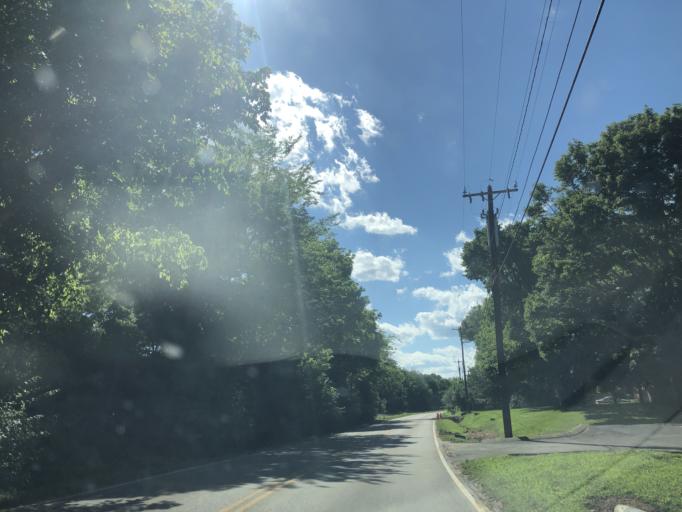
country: US
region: Tennessee
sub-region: Davidson County
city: Belle Meade
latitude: 36.0626
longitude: -86.9337
